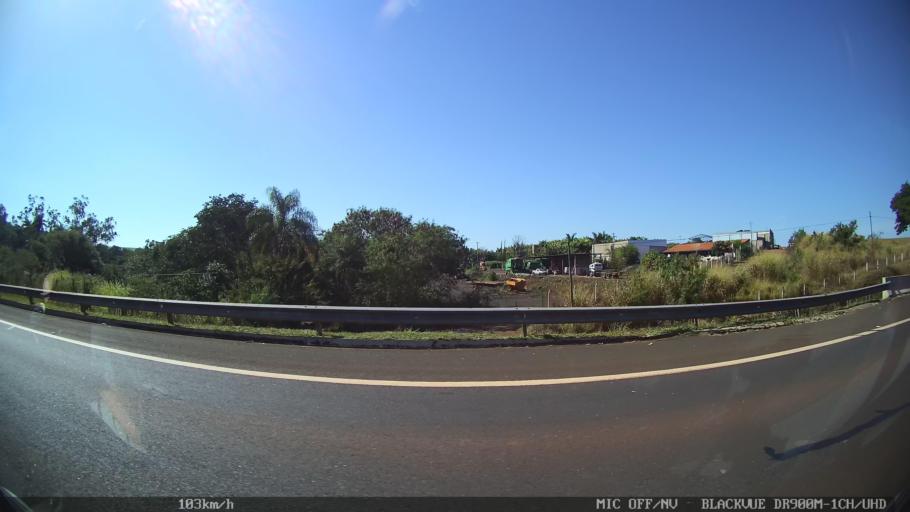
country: BR
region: Sao Paulo
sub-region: Batatais
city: Batatais
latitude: -20.8528
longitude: -47.6011
